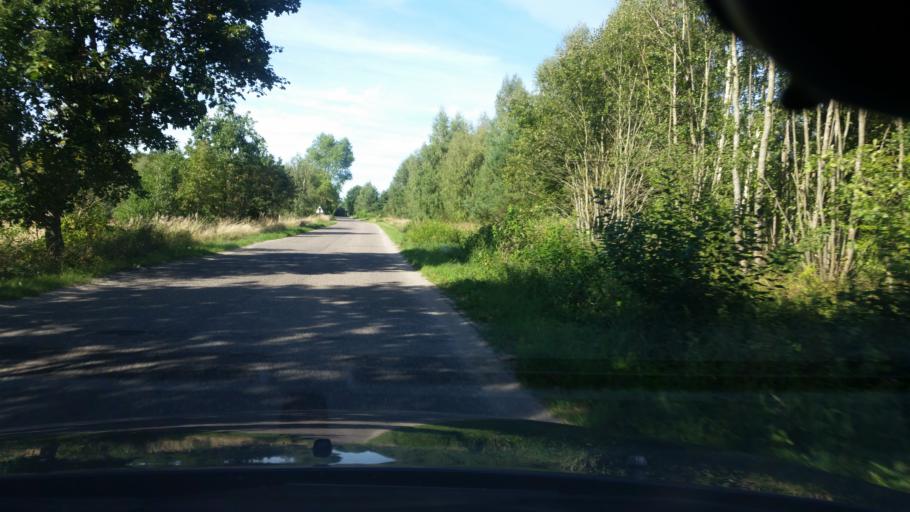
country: PL
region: Pomeranian Voivodeship
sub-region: Powiat wejherowski
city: Choczewo
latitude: 54.7613
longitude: 17.7922
